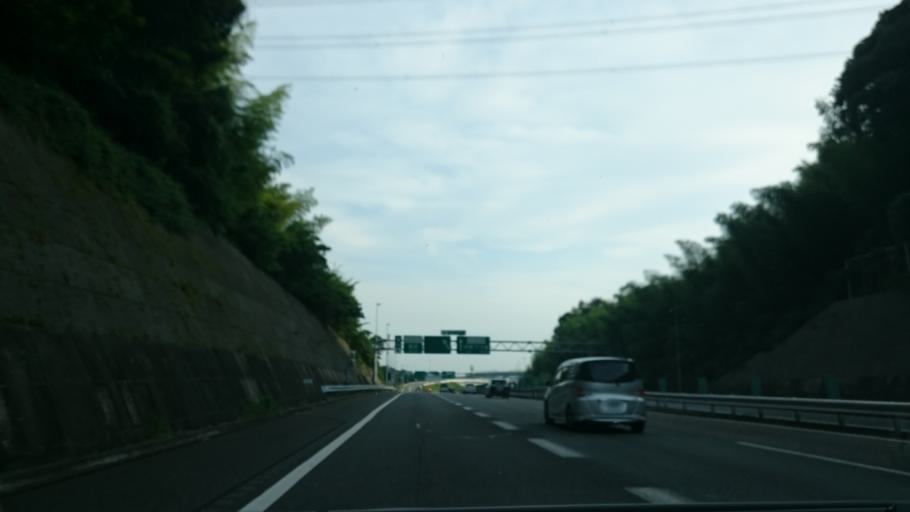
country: JP
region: Mie
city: Yokkaichi
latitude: 35.0440
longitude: 136.6324
